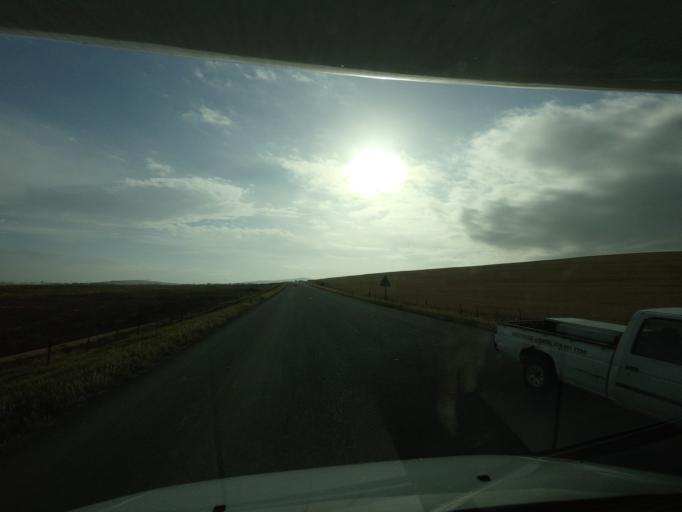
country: ZA
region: Western Cape
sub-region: City of Cape Town
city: Sunset Beach
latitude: -33.7251
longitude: 18.4919
